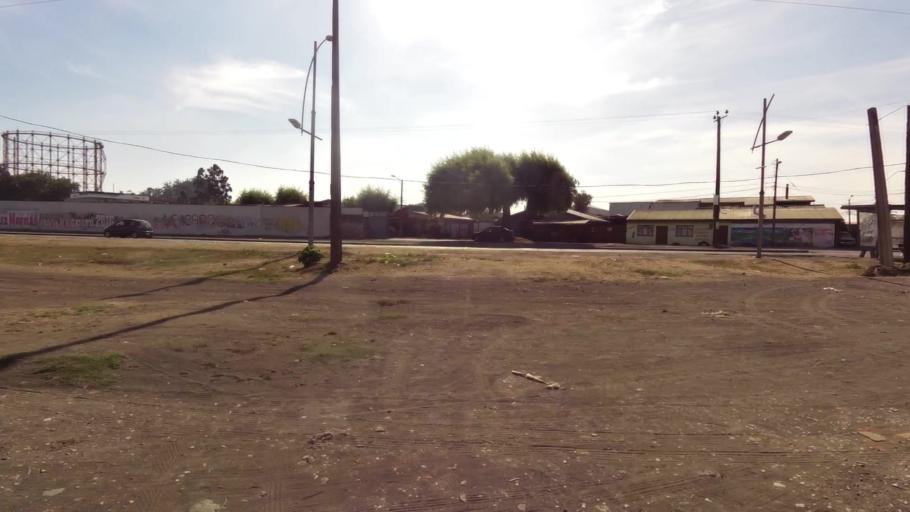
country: CL
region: Biobio
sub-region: Provincia de Concepcion
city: Talcahuano
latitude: -36.7779
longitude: -73.1130
